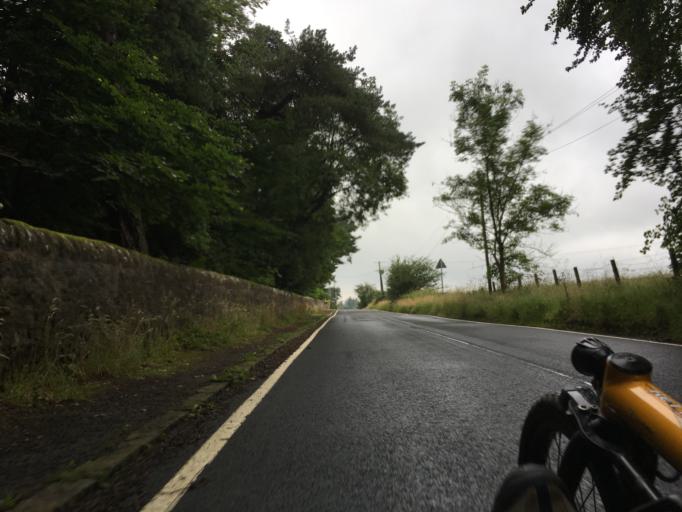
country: GB
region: Scotland
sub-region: West Lothian
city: West Calder
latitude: 55.8387
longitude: -3.5305
